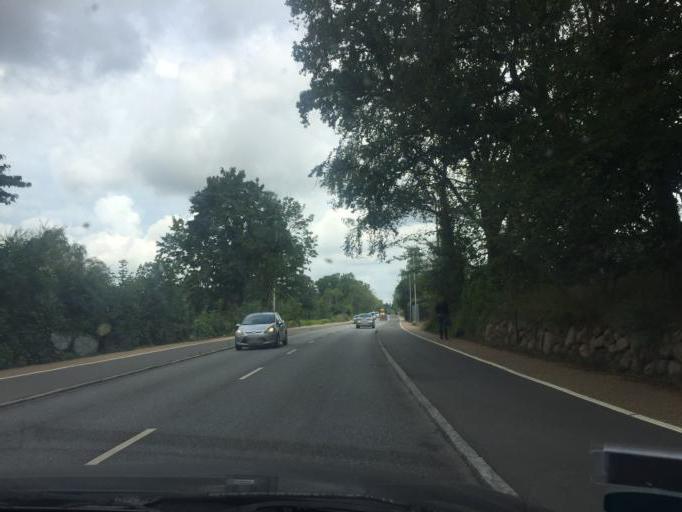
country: DK
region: Capital Region
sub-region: Allerod Kommune
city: Lillerod
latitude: 55.8738
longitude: 12.3550
